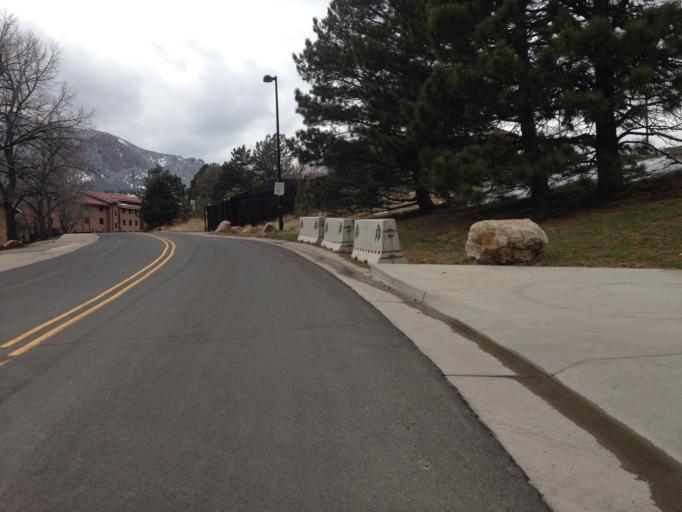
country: US
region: Colorado
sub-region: Boulder County
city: Boulder
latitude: 40.0038
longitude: -105.2613
